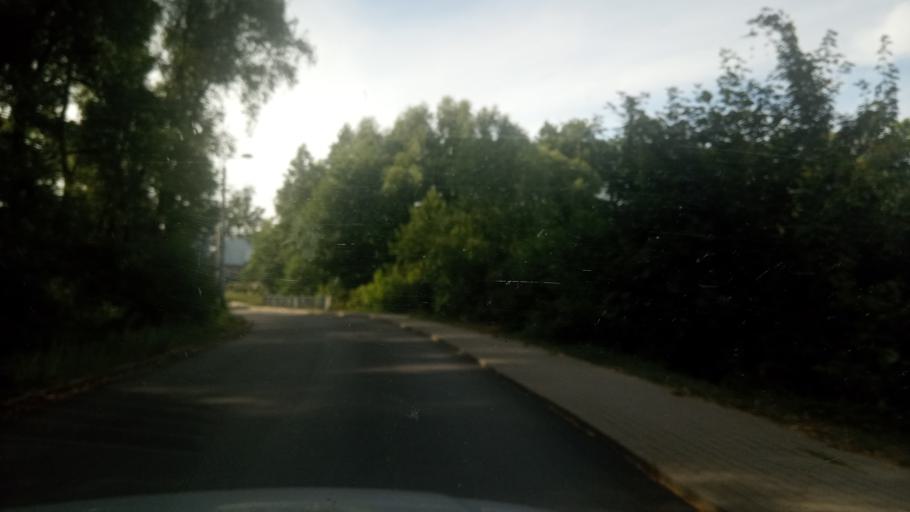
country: PL
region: Kujawsko-Pomorskie
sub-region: Powiat nakielski
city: Sadki
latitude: 53.1939
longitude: 17.3911
